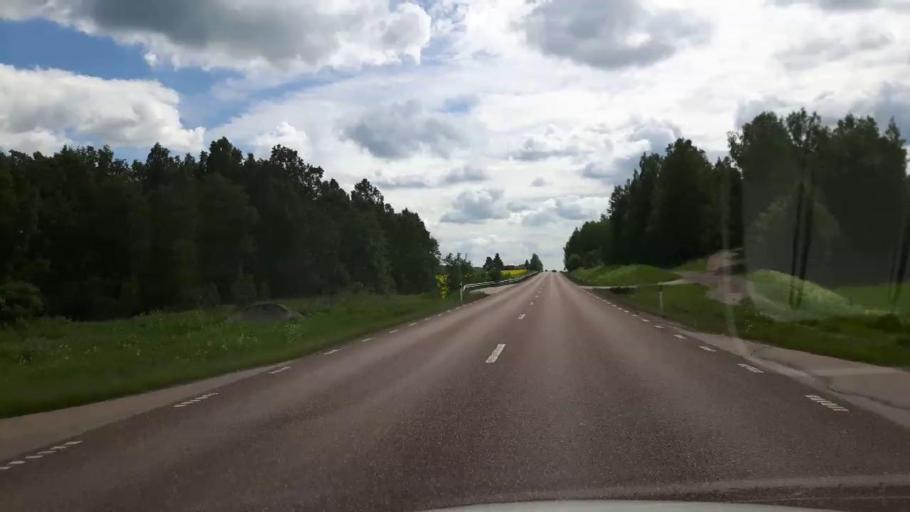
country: SE
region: Dalarna
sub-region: Hedemora Kommun
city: Langshyttan
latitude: 60.3815
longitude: 15.9091
